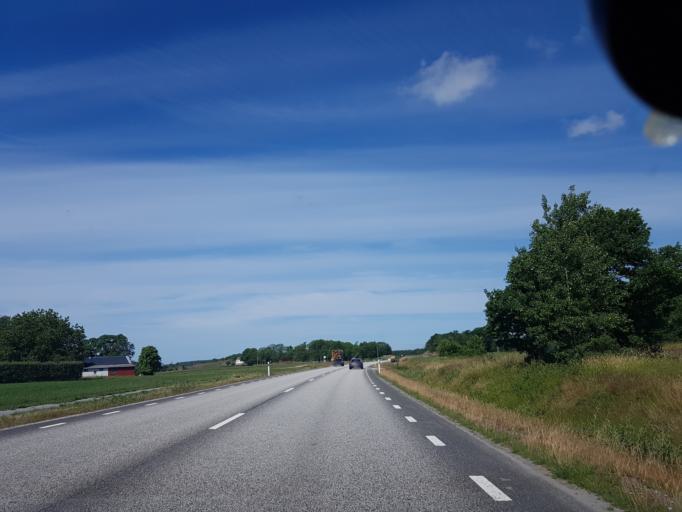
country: SE
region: Vaestra Goetaland
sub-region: Orust
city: Henan
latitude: 58.1458
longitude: 11.6060
